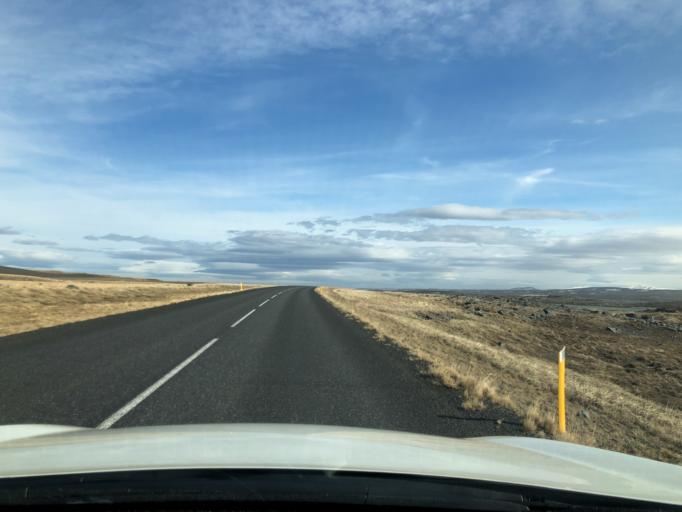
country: IS
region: Northeast
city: Laugar
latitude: 65.7498
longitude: -16.3850
